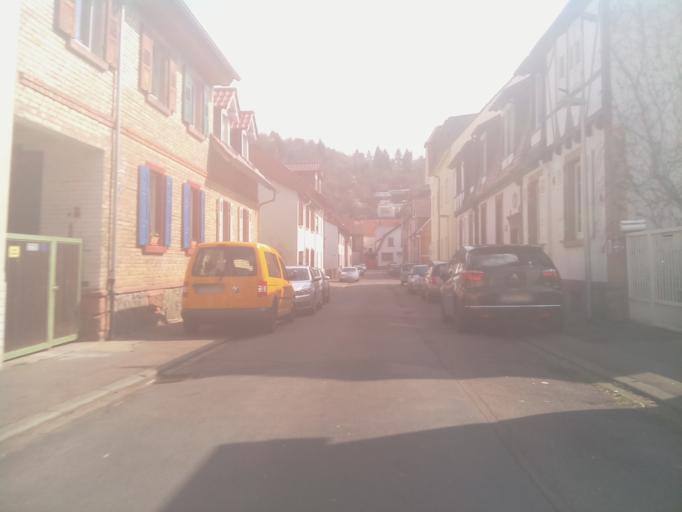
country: DE
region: Baden-Wuerttemberg
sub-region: Karlsruhe Region
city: Weinheim
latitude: 49.5566
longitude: 8.6719
